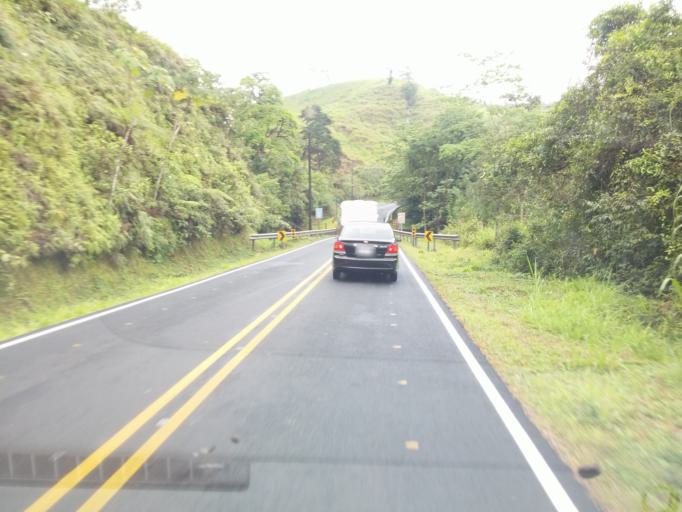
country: CR
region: Alajuela
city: San Ramon
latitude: 10.2101
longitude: -84.5416
